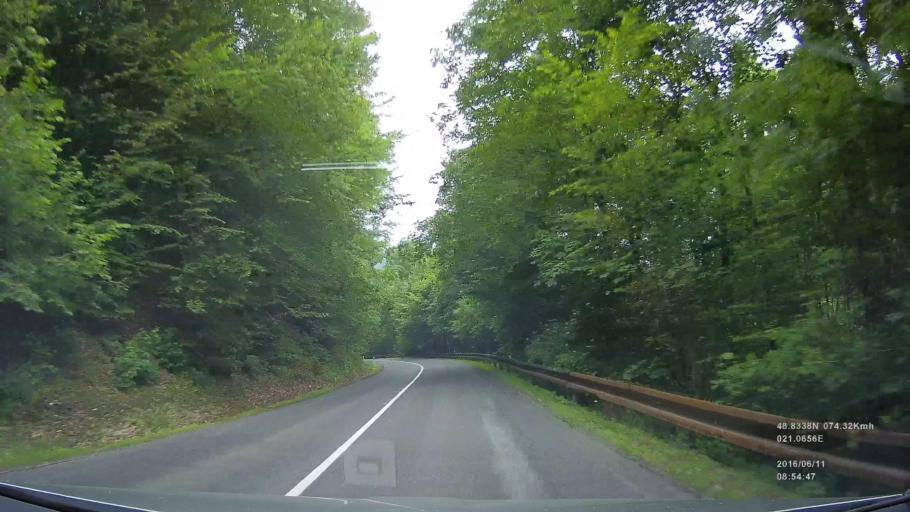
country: SK
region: Kosicky
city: Gelnica
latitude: 48.8341
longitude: 21.0719
